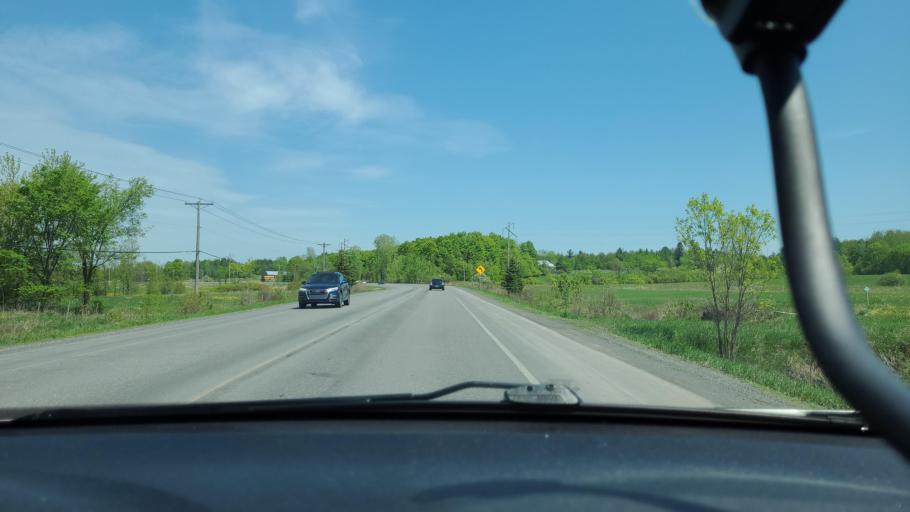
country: CA
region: Quebec
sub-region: Laurentides
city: Saint-Colomban
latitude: 45.6688
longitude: -74.2125
